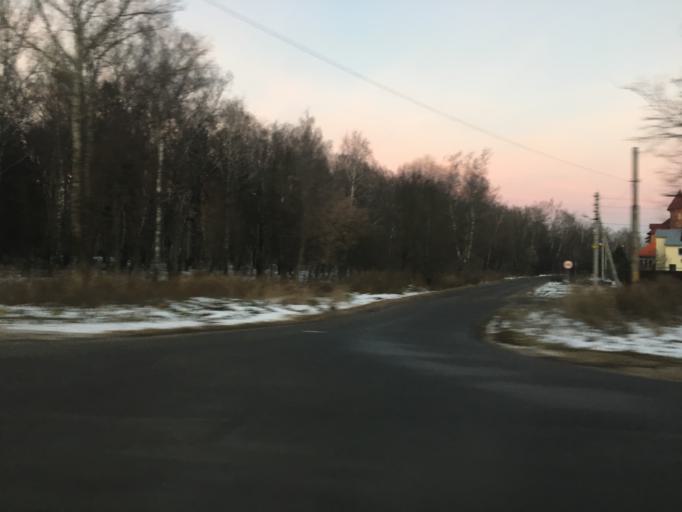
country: RU
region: Tula
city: Gorelki
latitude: 54.2504
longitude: 37.6117
